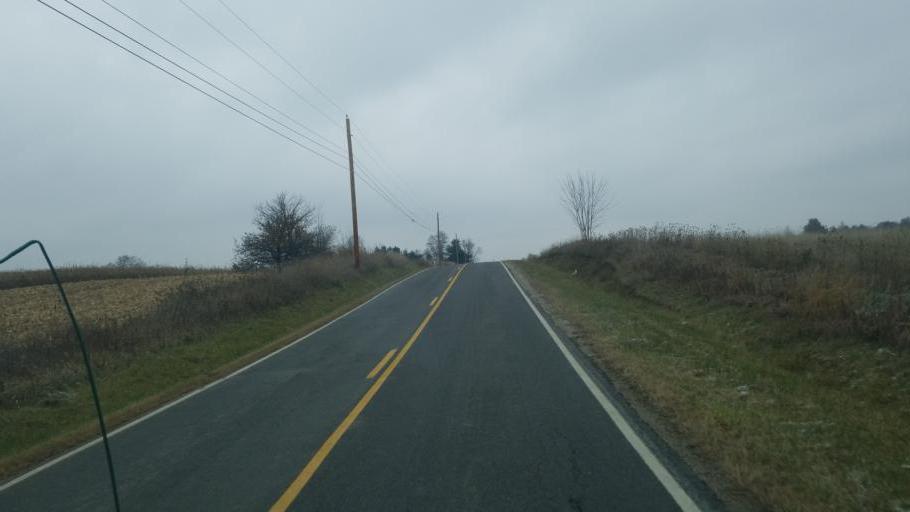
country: US
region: Ohio
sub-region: Medina County
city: Lodi
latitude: 41.1309
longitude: -82.0019
